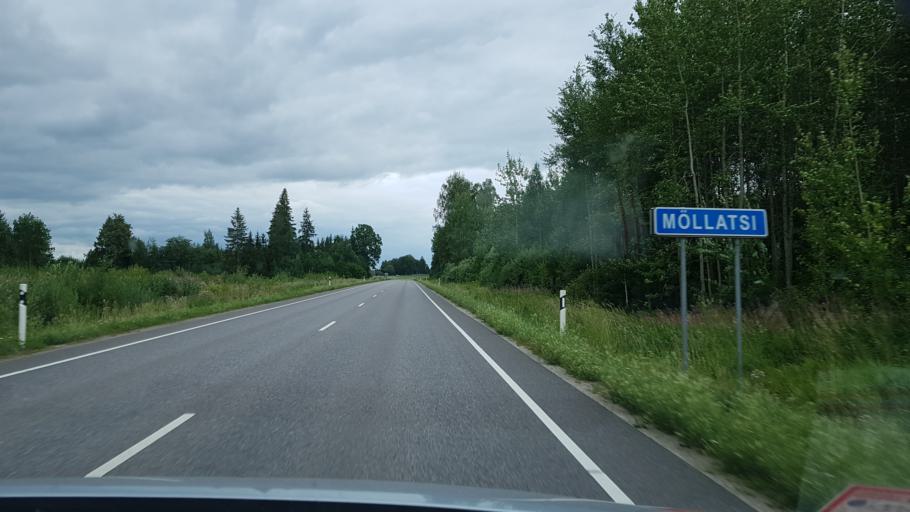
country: EE
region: Tartu
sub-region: Tartu linn
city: Tartu
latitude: 58.4391
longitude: 26.8243
